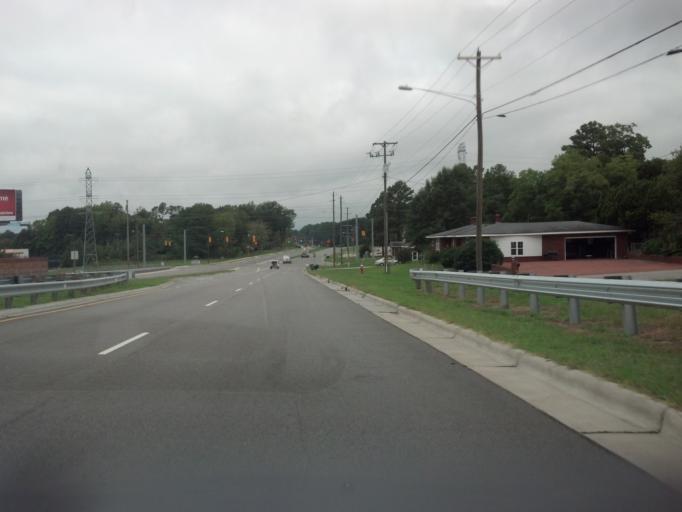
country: US
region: North Carolina
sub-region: Nash County
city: Rocky Mount
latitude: 35.9685
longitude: -77.8147
